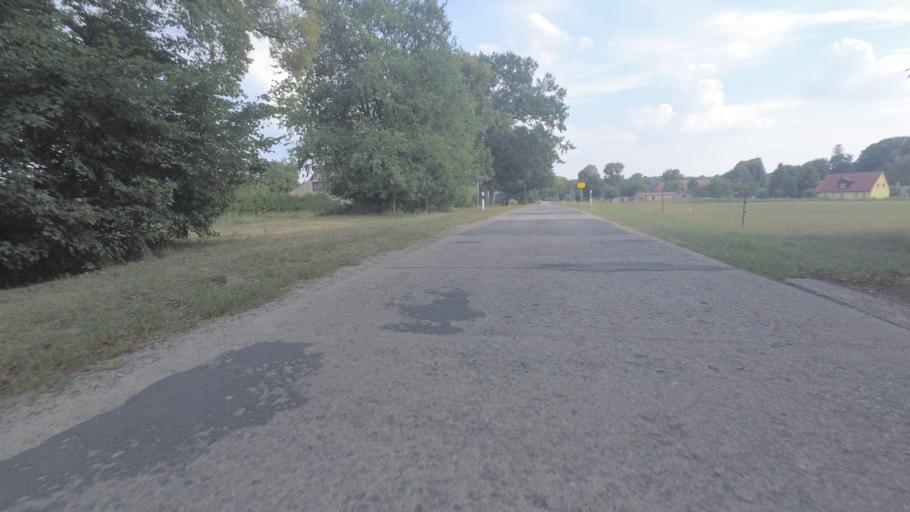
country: DE
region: Brandenburg
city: Wittstock
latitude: 53.2620
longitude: 12.4619
